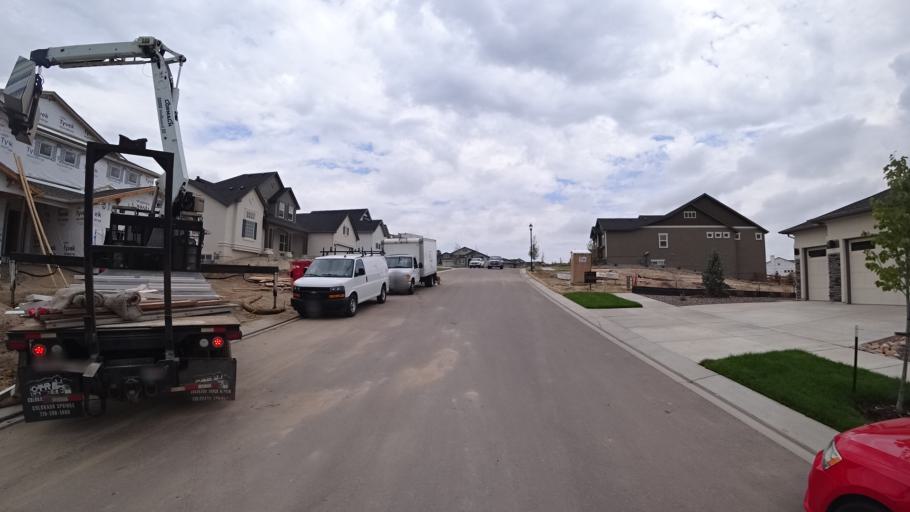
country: US
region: Colorado
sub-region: El Paso County
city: Gleneagle
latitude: 39.0084
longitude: -104.7902
